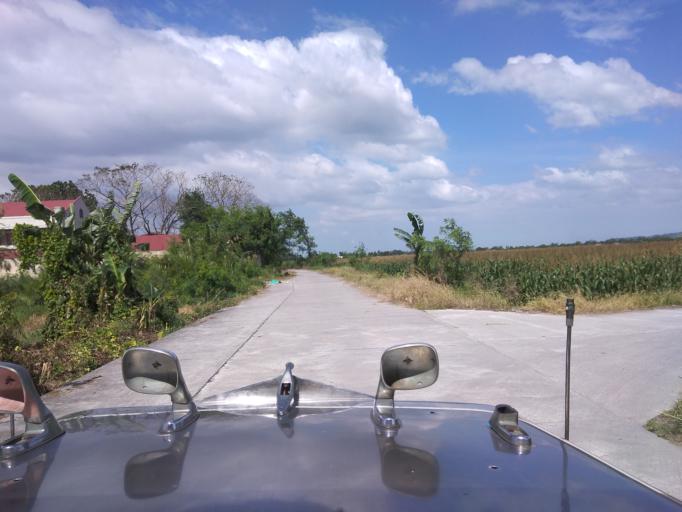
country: PH
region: Central Luzon
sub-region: Province of Pampanga
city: Anao
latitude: 15.1285
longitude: 120.7004
